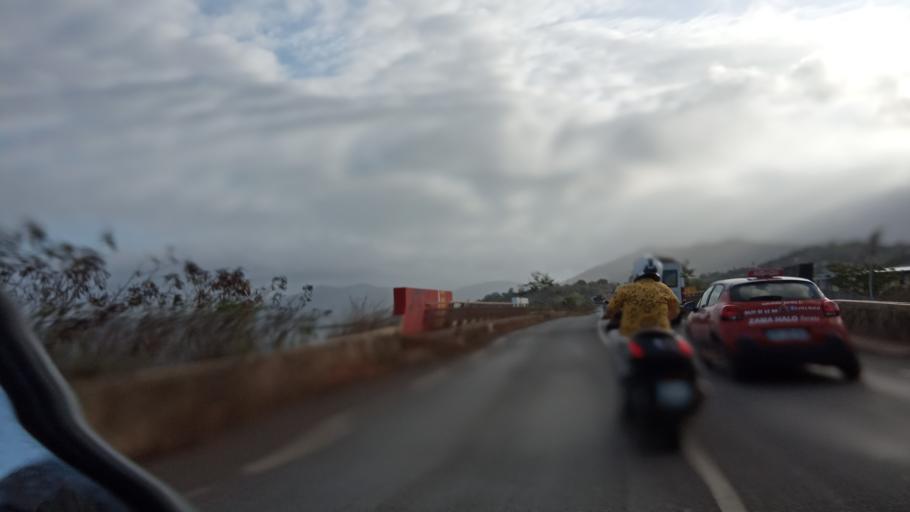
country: YT
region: Mamoudzou
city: Mamoudzou
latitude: -12.7908
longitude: 45.2229
